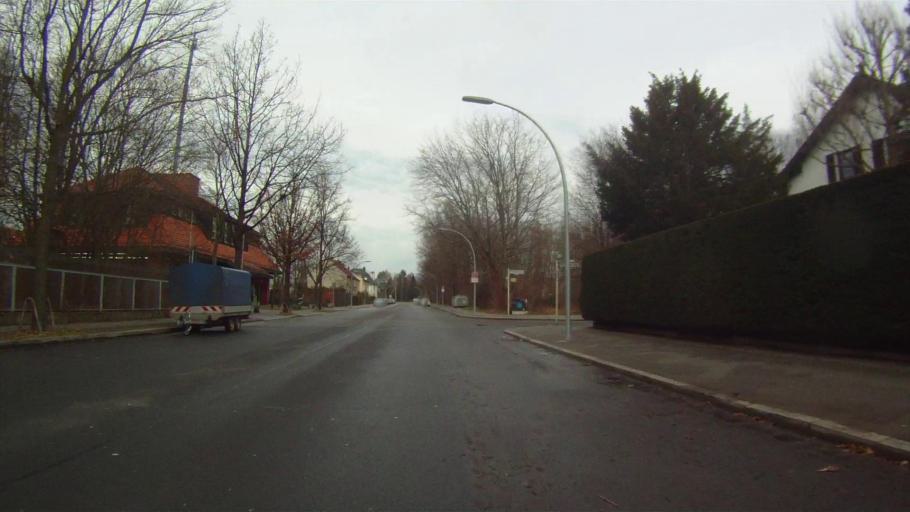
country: DE
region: Berlin
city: Lichtenrade
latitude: 52.3922
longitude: 13.4125
